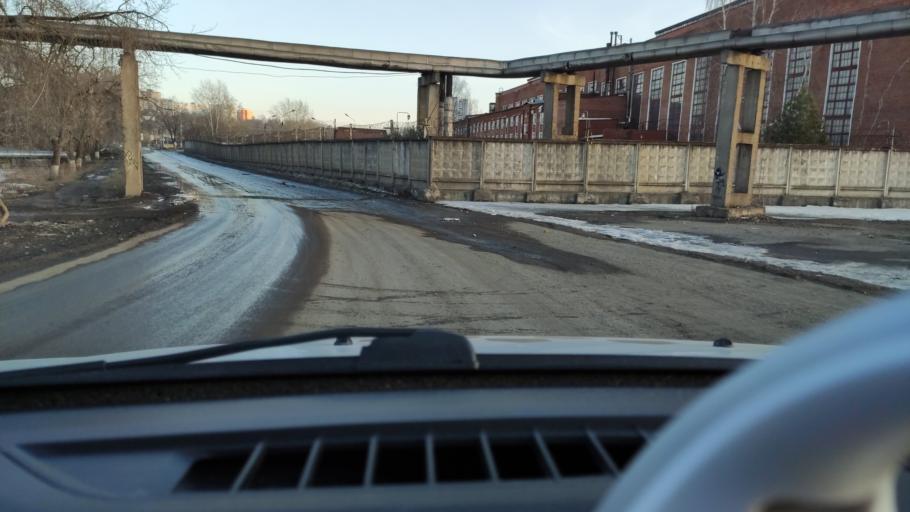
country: RU
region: Perm
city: Perm
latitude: 58.0403
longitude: 56.3062
